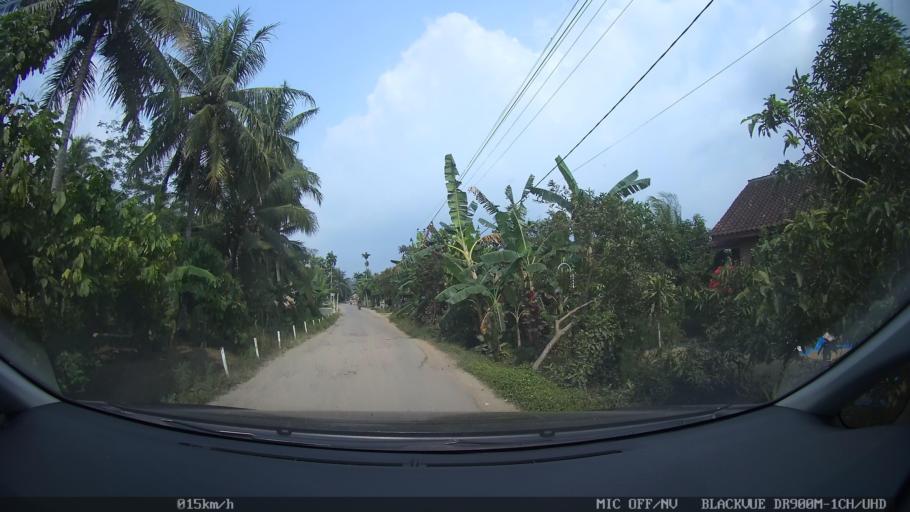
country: ID
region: Lampung
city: Kedondong
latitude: -5.4096
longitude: 105.0054
